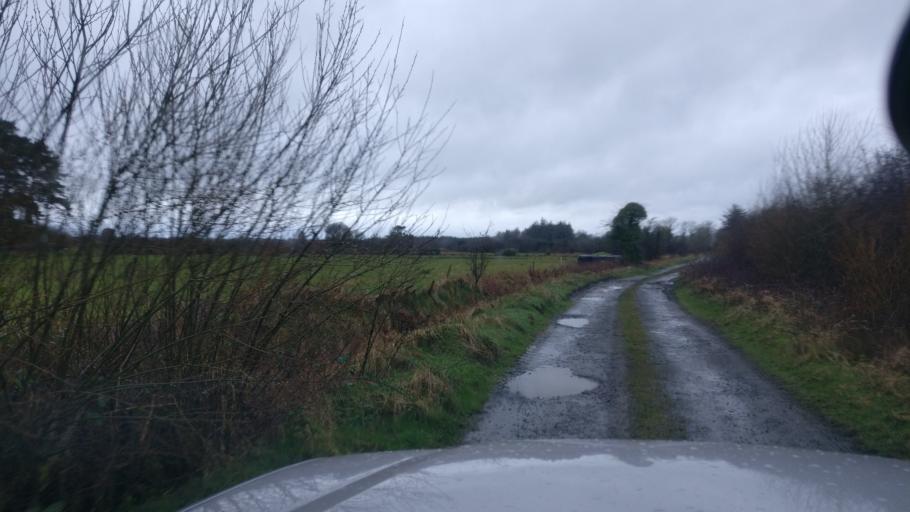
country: IE
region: Connaught
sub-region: County Galway
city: Ballinasloe
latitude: 53.2507
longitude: -8.3286
